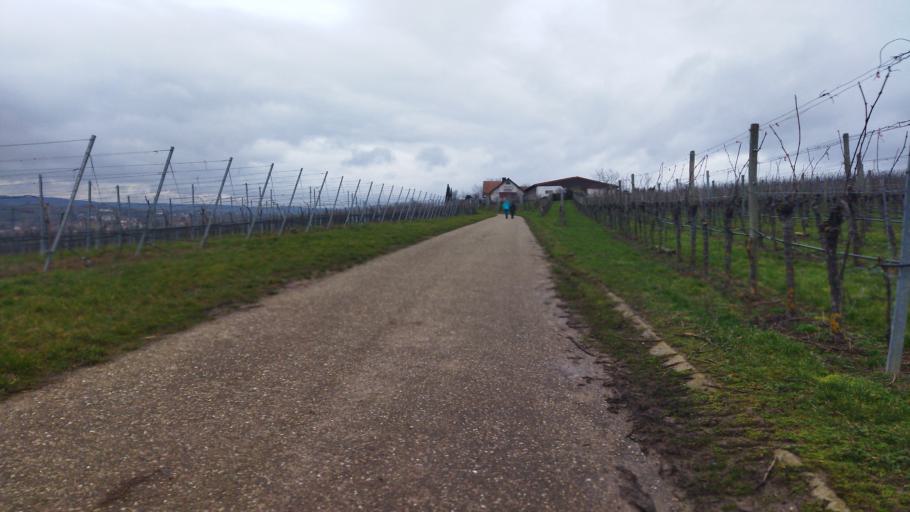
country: DE
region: Baden-Wuerttemberg
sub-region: Regierungsbezirk Stuttgart
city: Talheim
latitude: 49.0693
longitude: 9.1780
